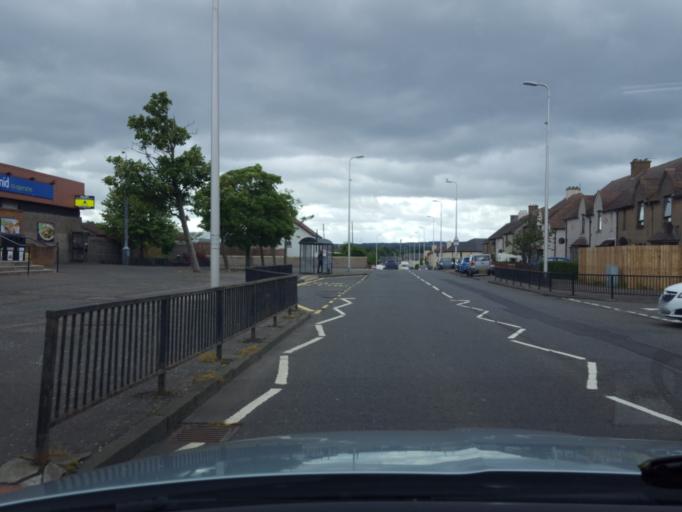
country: GB
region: Scotland
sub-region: West Lothian
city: Blackburn
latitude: 55.8748
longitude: -3.6240
